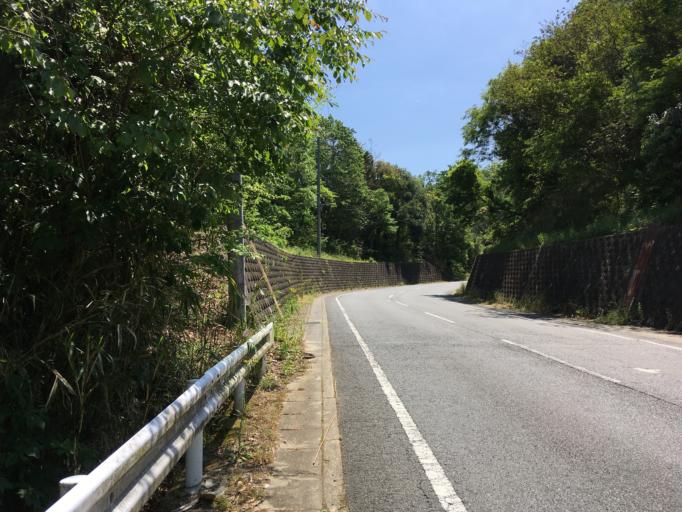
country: JP
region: Nara
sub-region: Ikoma-shi
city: Ikoma
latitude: 34.6522
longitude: 135.6873
